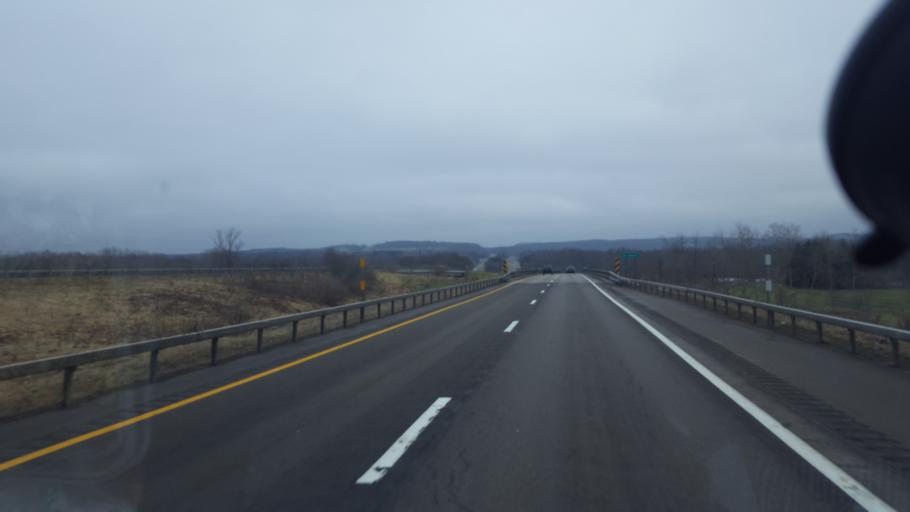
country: US
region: New York
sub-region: Chautauqua County
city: Falconer
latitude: 42.1394
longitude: -79.1122
